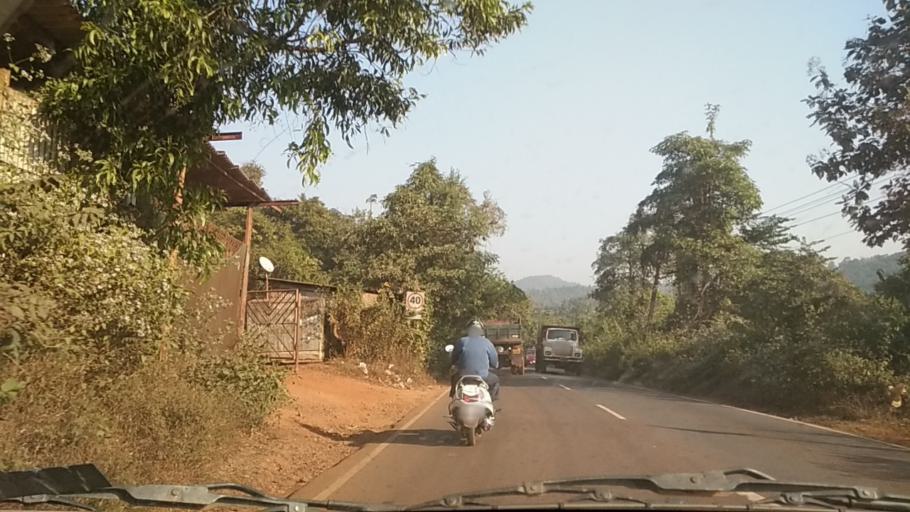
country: IN
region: Goa
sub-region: South Goa
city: Sanvordem
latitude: 15.2731
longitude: 74.1205
